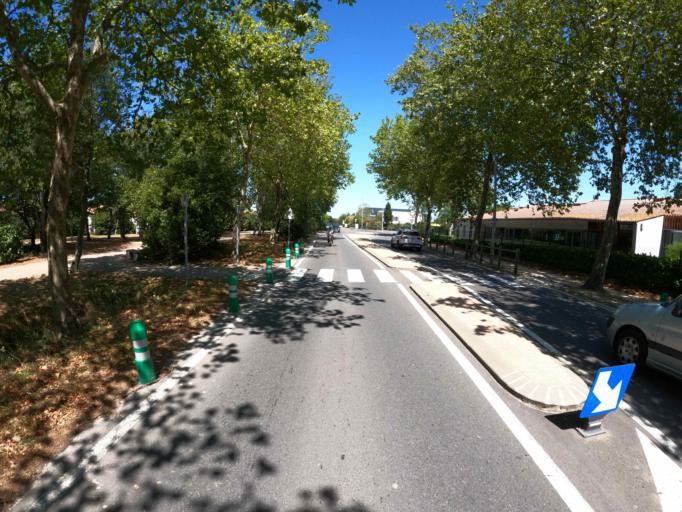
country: FR
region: Pays de la Loire
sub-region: Departement de la Vendee
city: Challans
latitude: 46.8387
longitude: -1.8658
